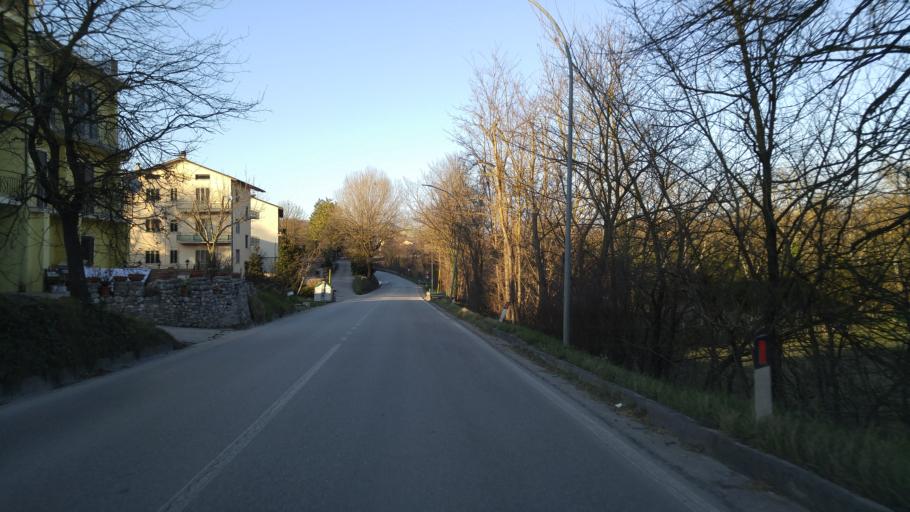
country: IT
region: The Marches
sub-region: Provincia di Pesaro e Urbino
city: Cagli
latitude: 43.5581
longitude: 12.6540
